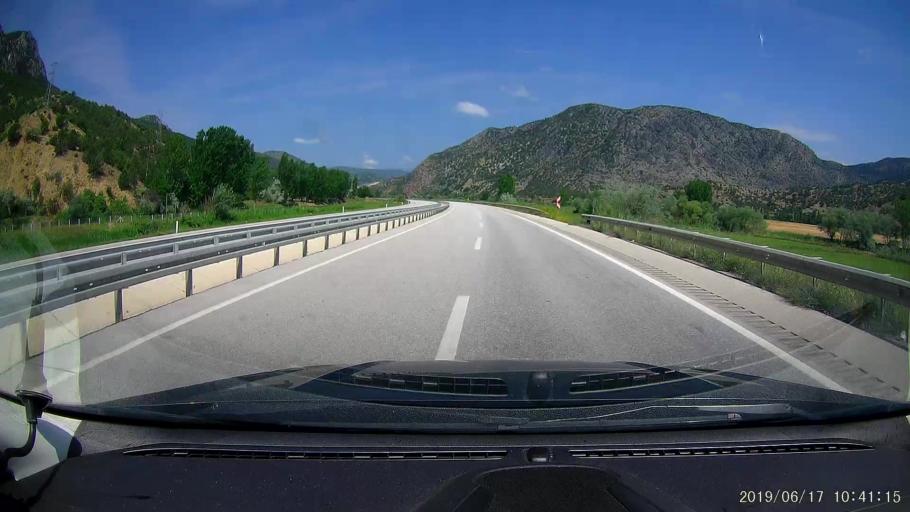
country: TR
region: Corum
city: Kargi
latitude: 41.0374
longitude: 34.5811
